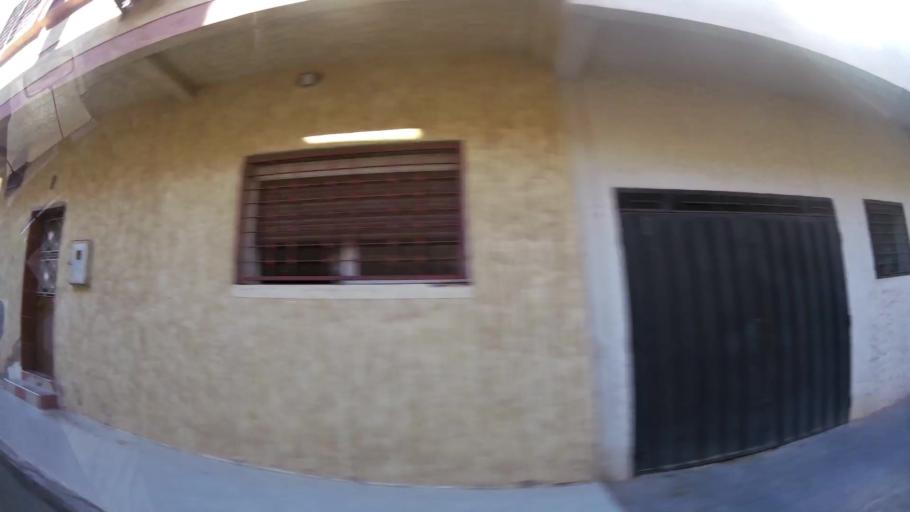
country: MA
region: Oriental
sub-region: Oujda-Angad
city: Oujda
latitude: 34.6631
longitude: -1.9053
